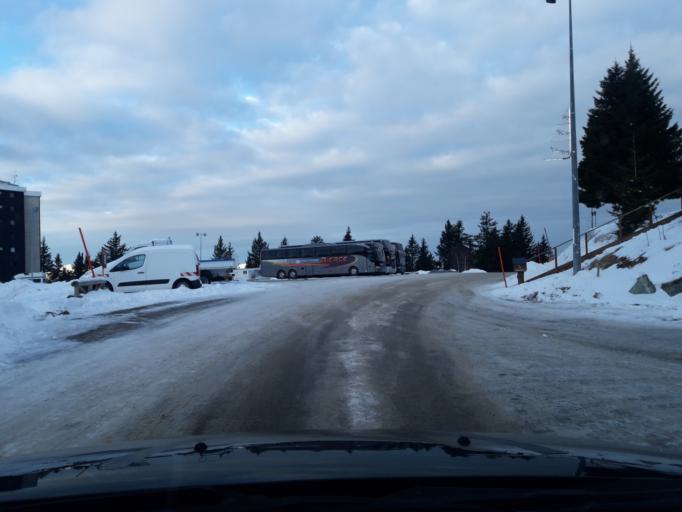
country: FR
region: Rhone-Alpes
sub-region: Departement de l'Isere
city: Vaulnaveys-le-Bas
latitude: 45.1264
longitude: 5.8749
